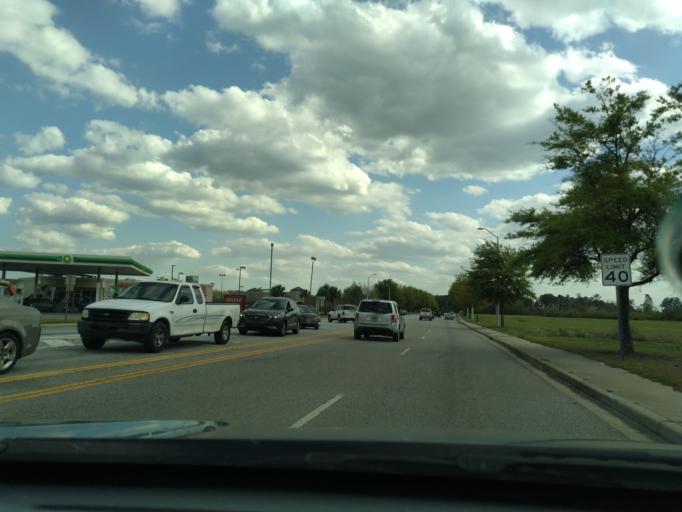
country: US
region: South Carolina
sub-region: Florence County
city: Florence
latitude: 34.1638
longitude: -79.7601
